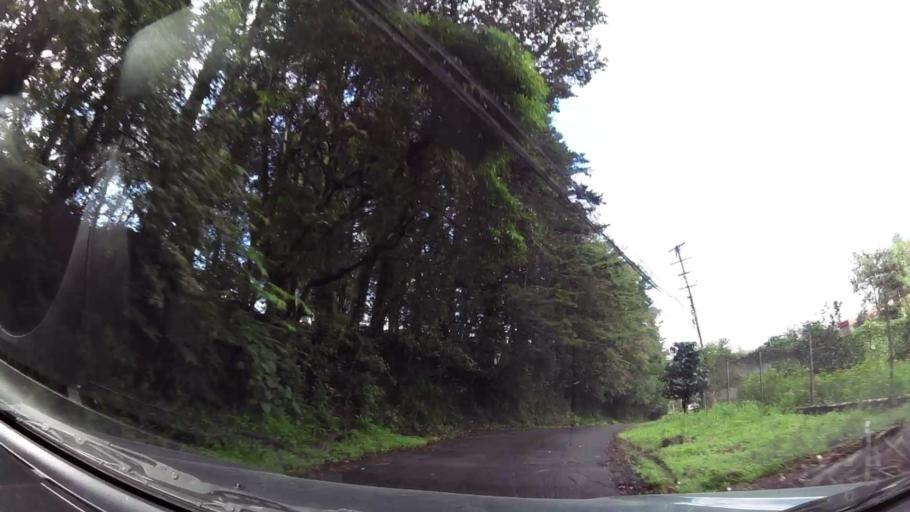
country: PA
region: Chiriqui
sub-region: Distrito Boquete
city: Boquete
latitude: 8.7953
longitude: -82.4371
